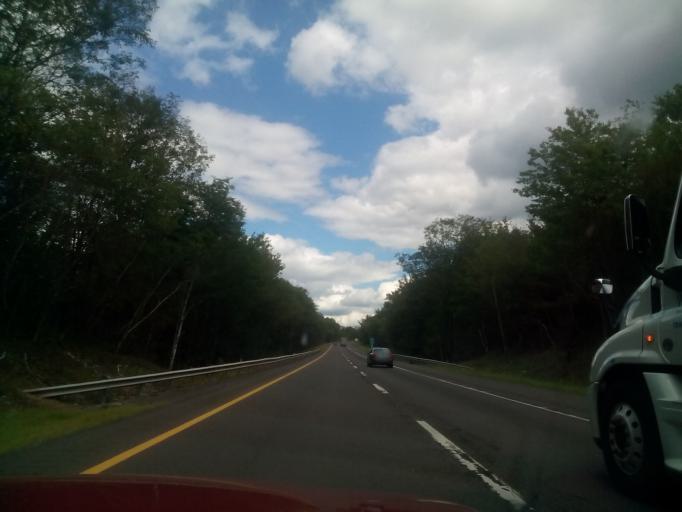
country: US
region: Pennsylvania
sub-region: Luzerne County
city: White Haven
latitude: 41.0721
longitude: -75.6817
